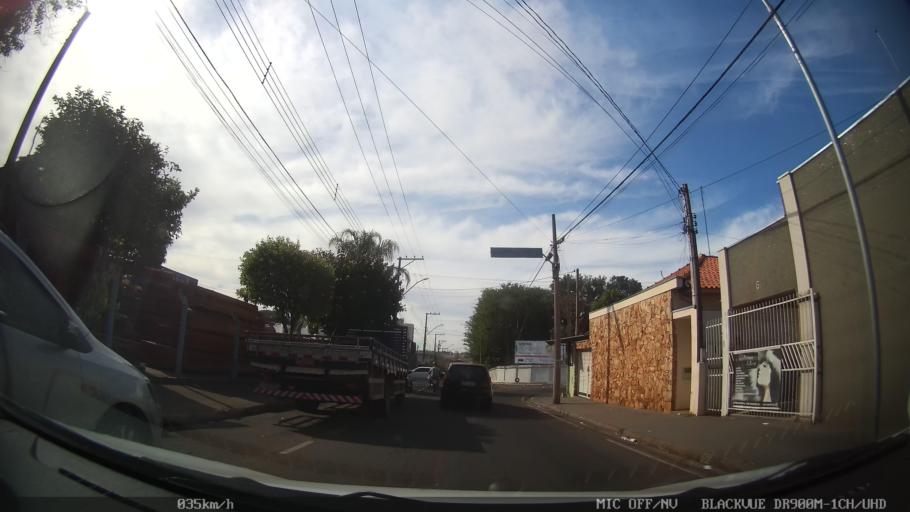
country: BR
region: Sao Paulo
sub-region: Catanduva
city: Catanduva
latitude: -21.1295
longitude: -48.9747
